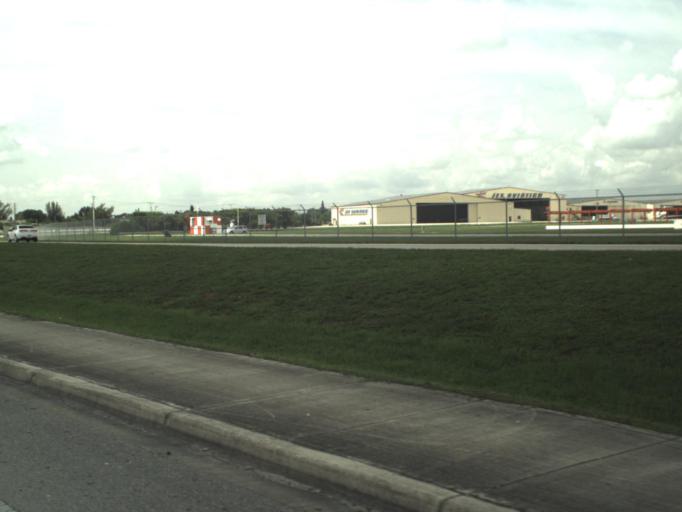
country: US
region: Florida
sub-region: Palm Beach County
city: Lake Clarke Shores
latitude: 26.6821
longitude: -80.0739
